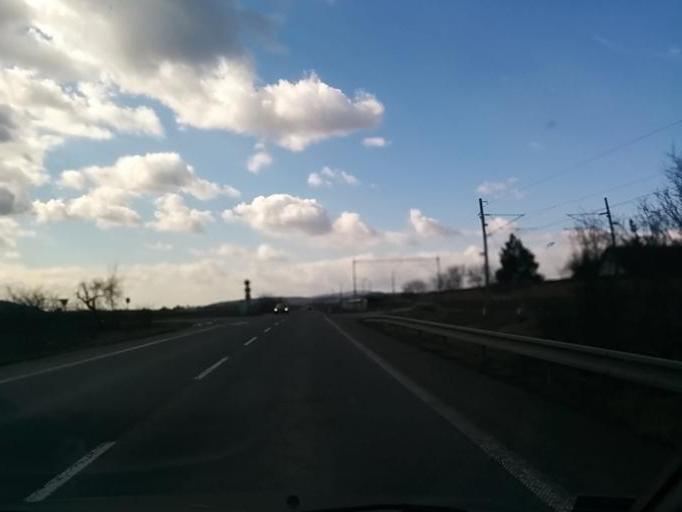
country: SK
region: Trenciansky
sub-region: Okres Trencin
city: Trencin
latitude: 48.8502
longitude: 17.9412
